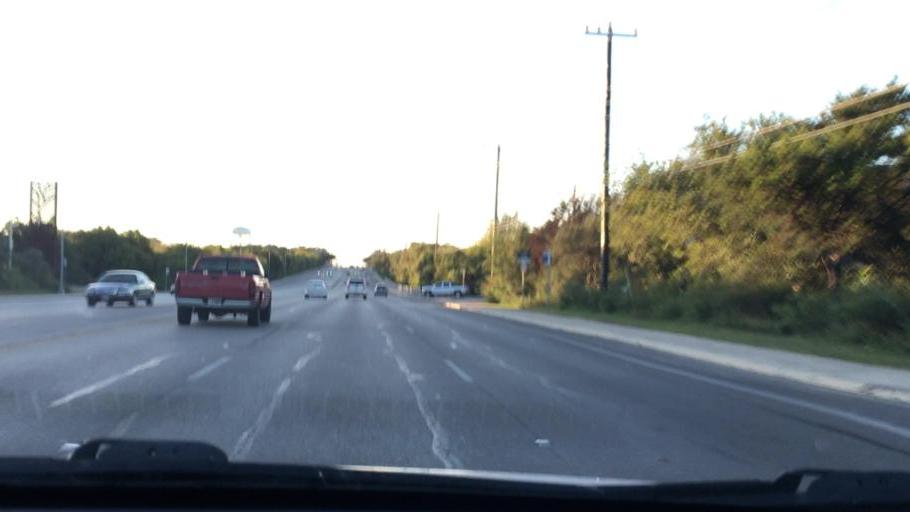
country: US
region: Texas
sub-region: Bexar County
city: Castle Hills
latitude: 29.5524
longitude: -98.5329
